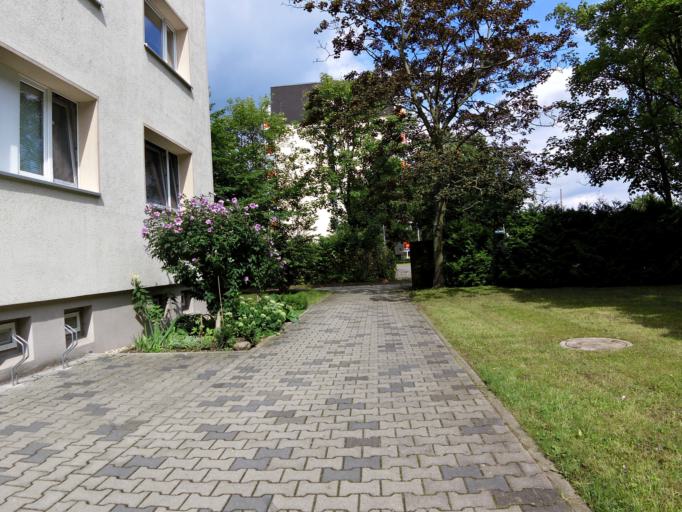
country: DE
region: Saxony
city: Rackwitz
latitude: 51.3834
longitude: 12.4198
